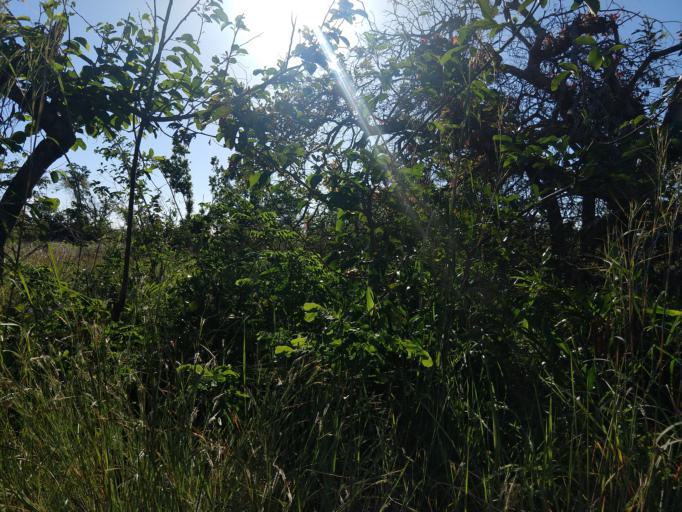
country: MZ
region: Sofala
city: Beira
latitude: -19.5714
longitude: 35.2501
